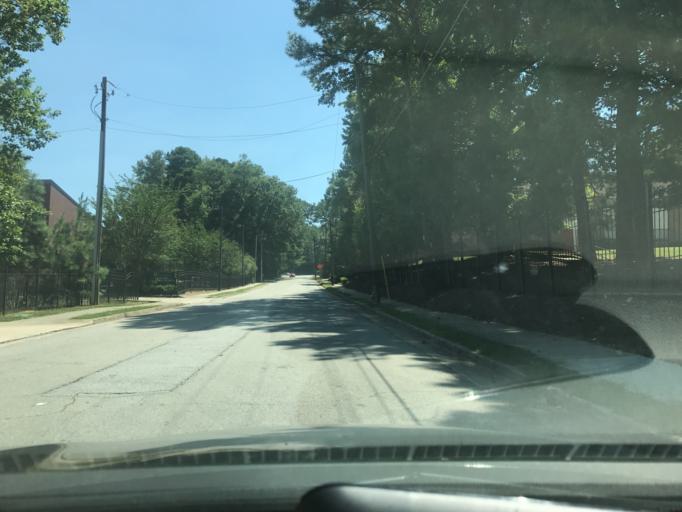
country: US
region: Georgia
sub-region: Fulton County
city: East Point
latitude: 33.7550
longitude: -84.4931
